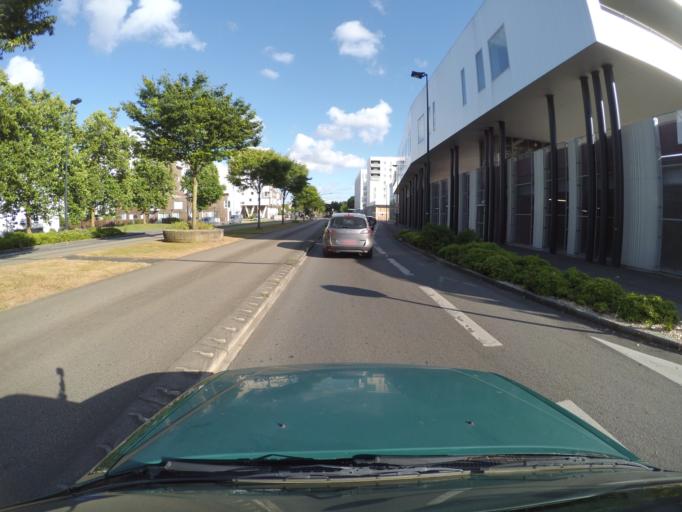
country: FR
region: Pays de la Loire
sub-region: Departement de la Loire-Atlantique
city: Reze
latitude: 47.1950
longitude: -1.5298
